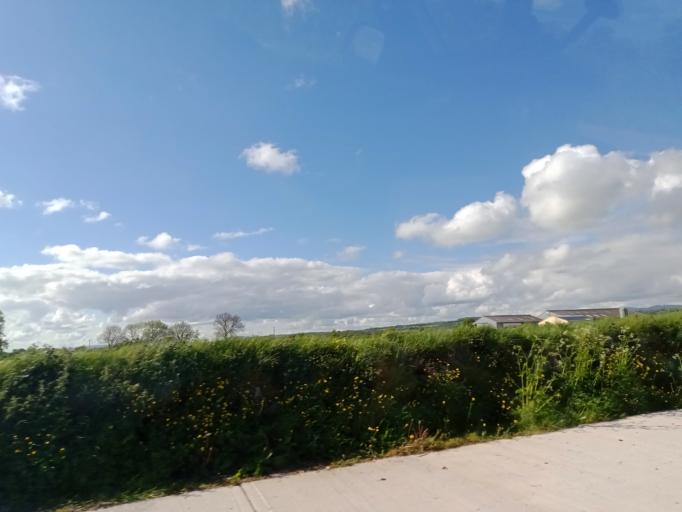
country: IE
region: Munster
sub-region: County Cork
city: Fermoy
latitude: 52.1580
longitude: -8.2740
